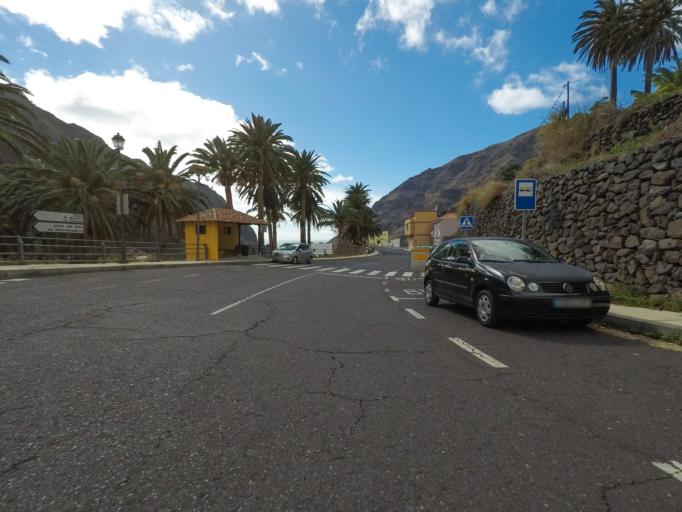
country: ES
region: Canary Islands
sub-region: Provincia de Santa Cruz de Tenerife
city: Vallehermosa
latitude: 28.1121
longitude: -17.3173
